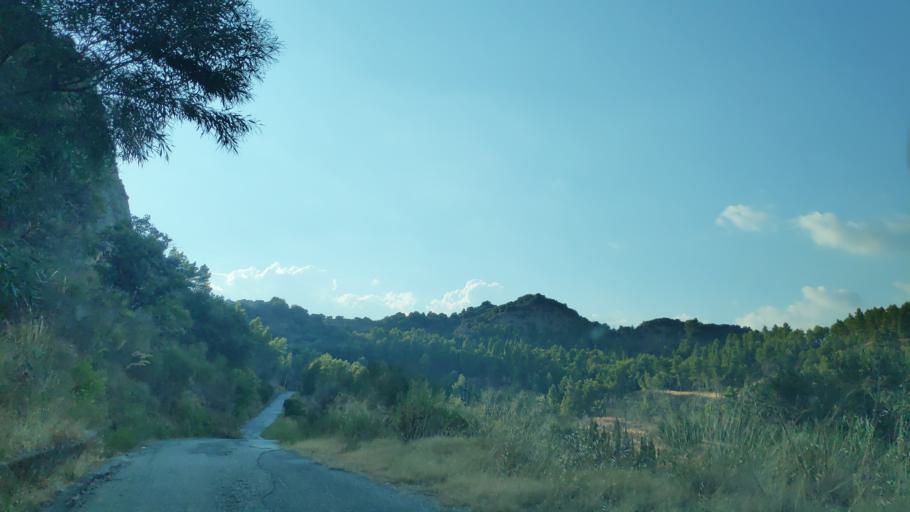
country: IT
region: Calabria
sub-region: Provincia di Reggio Calabria
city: Placanica
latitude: 38.4093
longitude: 16.4334
